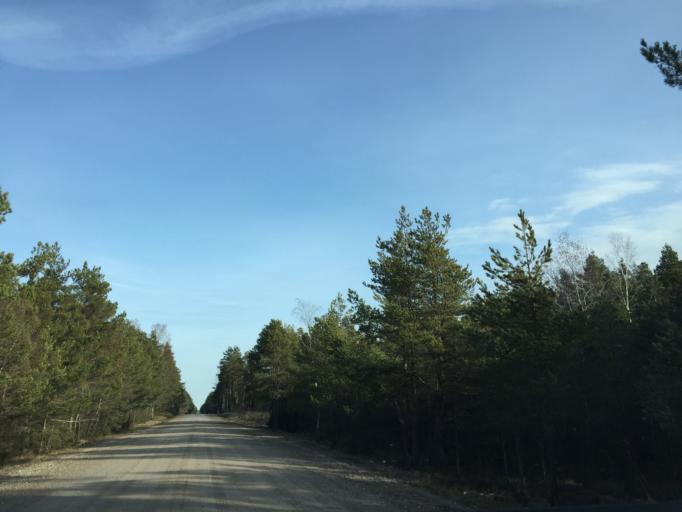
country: EE
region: Saare
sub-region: Kuressaare linn
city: Kuressaare
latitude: 58.3042
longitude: 21.9648
